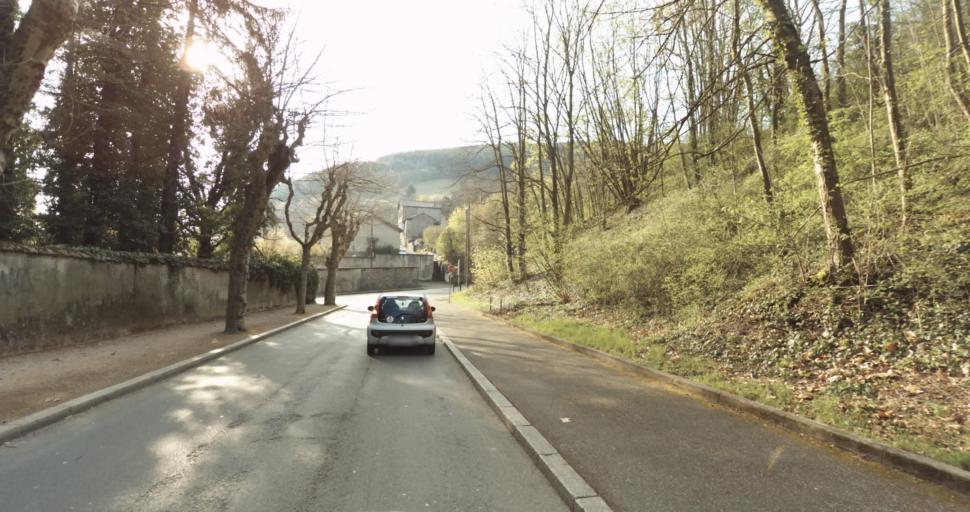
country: FR
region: Rhone-Alpes
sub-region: Departement du Rhone
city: Tarare
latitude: 45.8891
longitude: 4.4429
